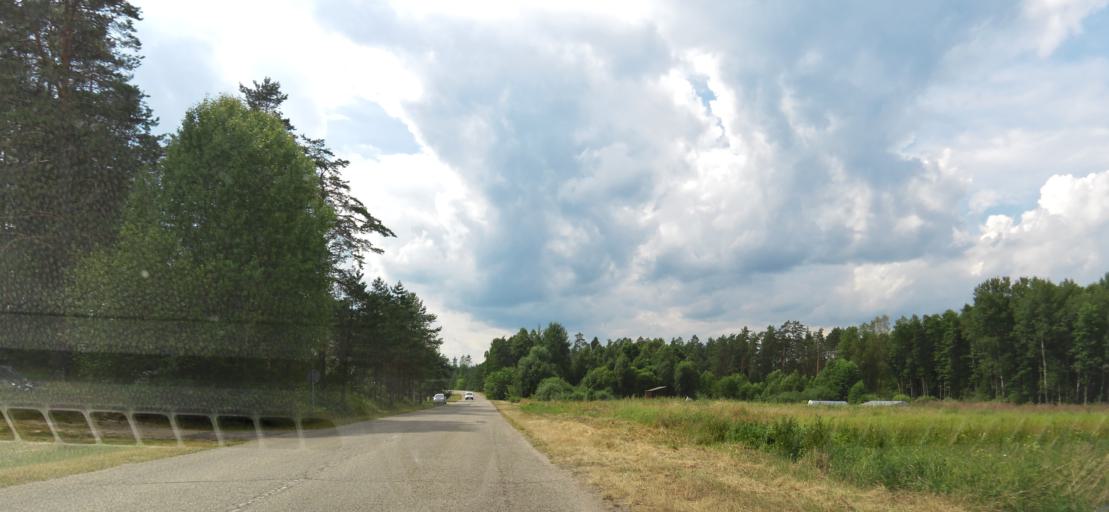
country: LT
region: Alytaus apskritis
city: Druskininkai
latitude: 53.9882
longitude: 24.0954
